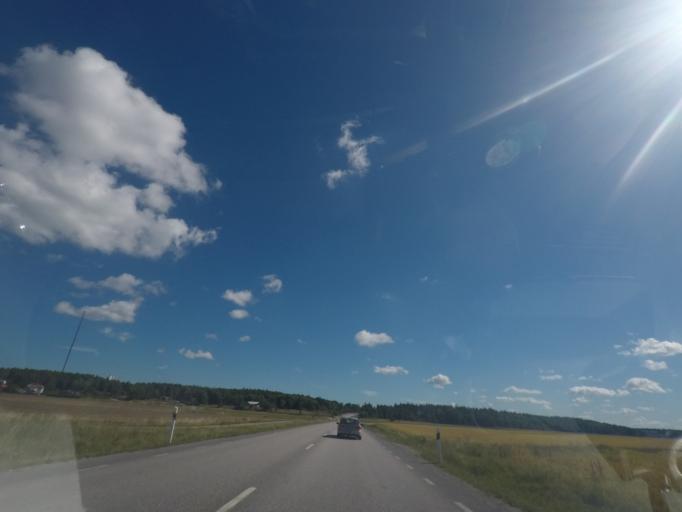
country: SE
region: Uppsala
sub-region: Uppsala Kommun
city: Saevja
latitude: 59.8470
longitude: 17.7650
